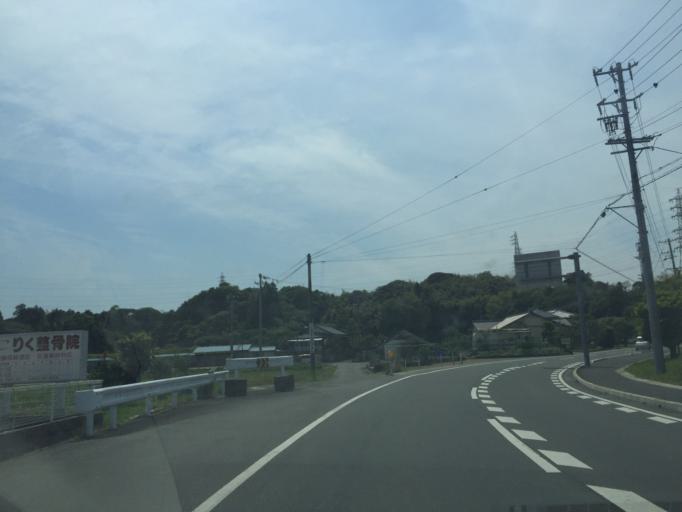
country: JP
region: Shizuoka
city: Kakegawa
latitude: 34.7811
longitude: 137.9662
